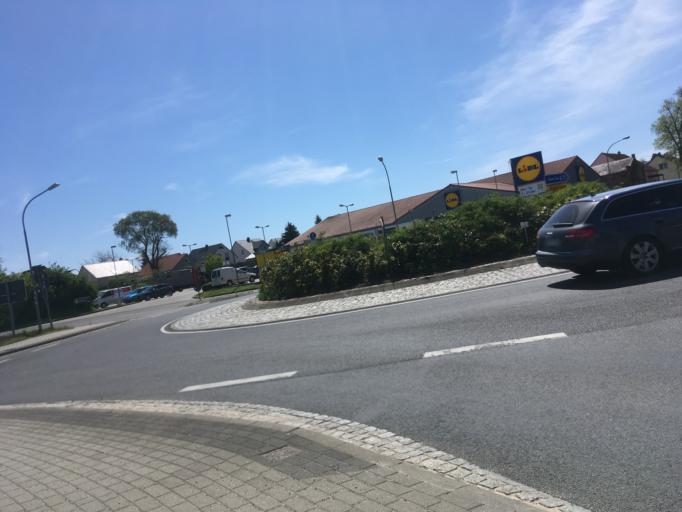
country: DE
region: Brandenburg
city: Wildau
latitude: 52.3234
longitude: 13.6152
